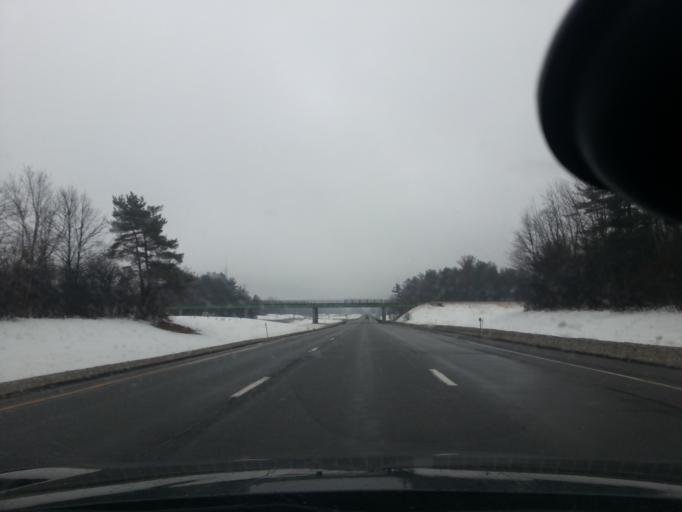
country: US
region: New York
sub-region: Jefferson County
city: Adams
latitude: 43.7126
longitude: -76.0763
